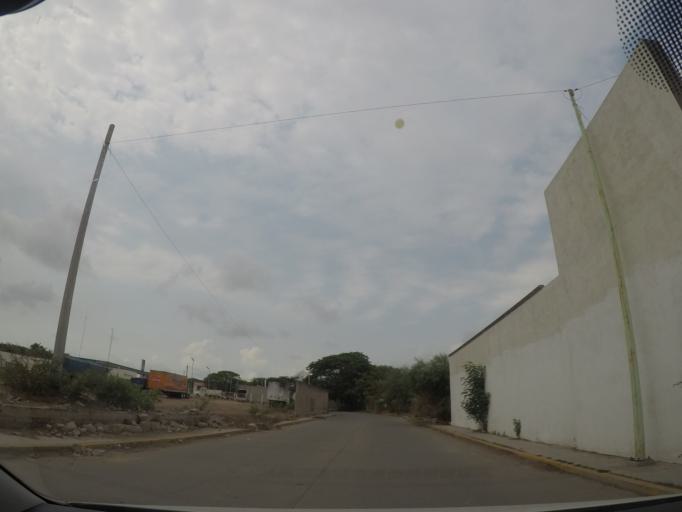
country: MX
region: Oaxaca
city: Juchitan de Zaragoza
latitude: 16.4491
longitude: -95.0148
